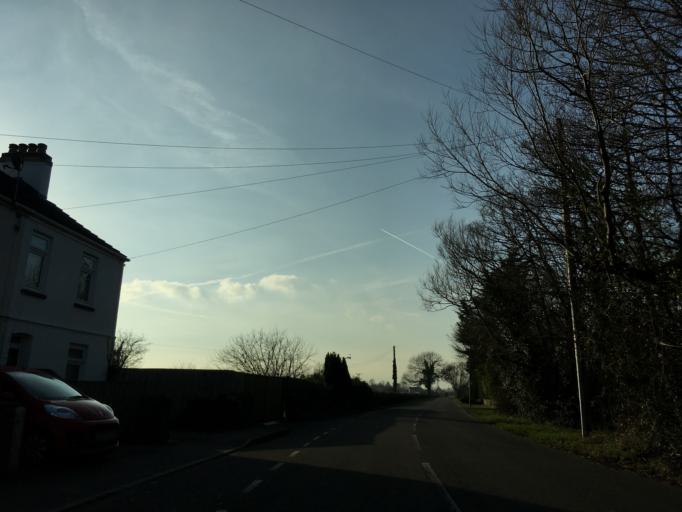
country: GB
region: Wales
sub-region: Newport
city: Goldcliff
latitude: 51.5634
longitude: -2.9181
